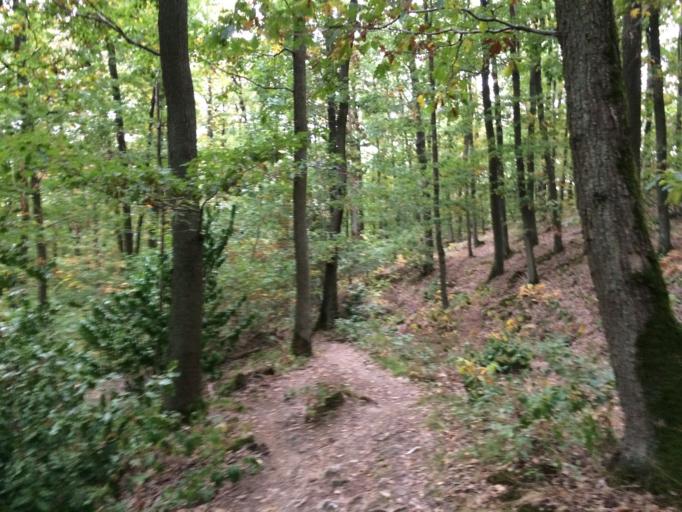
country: FR
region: Ile-de-France
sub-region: Departement de l'Essonne
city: Orsay
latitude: 48.6942
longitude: 2.2063
